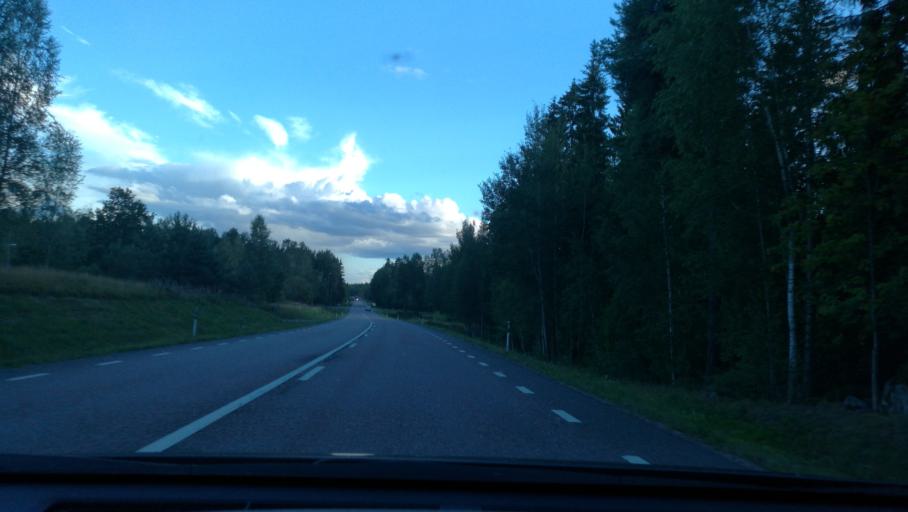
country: SE
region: Soedermanland
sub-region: Katrineholms Kommun
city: Katrineholm
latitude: 59.0392
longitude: 16.2169
